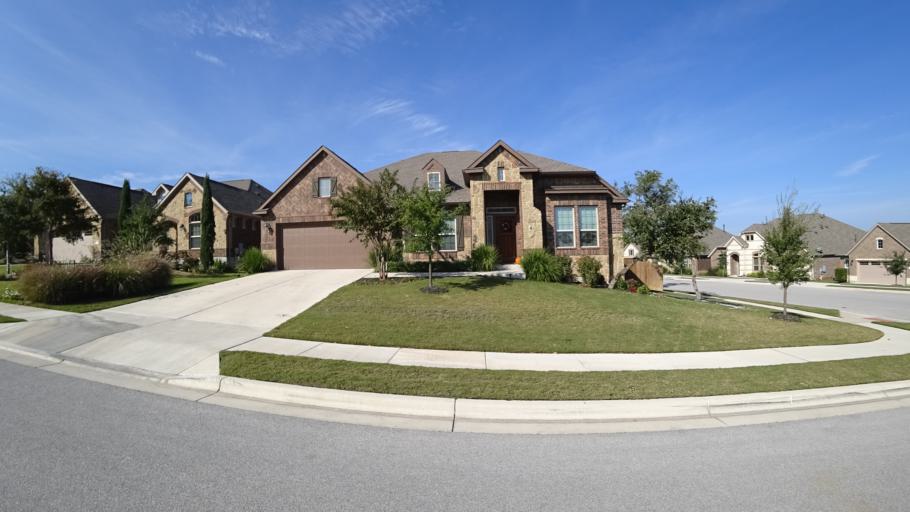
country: US
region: Texas
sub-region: Travis County
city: Barton Creek
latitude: 30.2299
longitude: -97.9084
